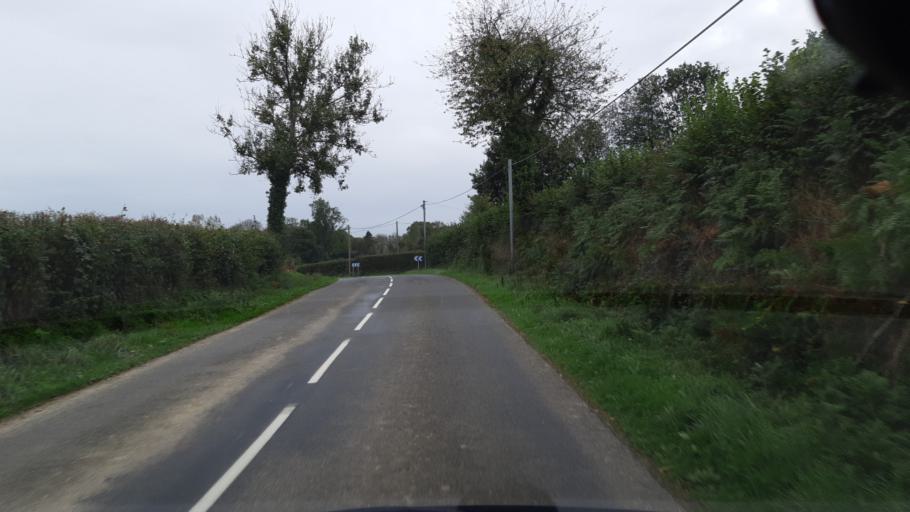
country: FR
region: Lower Normandy
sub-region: Departement de la Manche
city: Hambye
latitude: 48.9540
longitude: -1.2662
